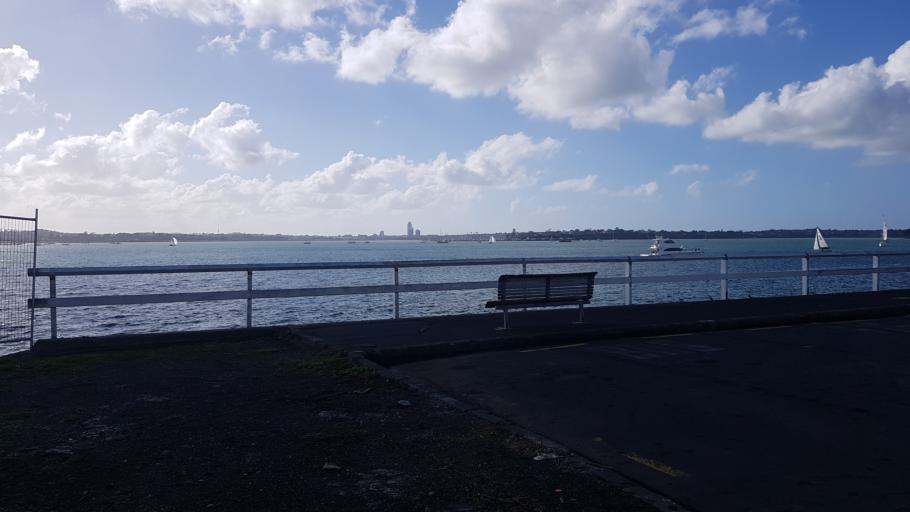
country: NZ
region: Auckland
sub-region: Auckland
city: Auckland
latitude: -36.8367
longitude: 174.7582
